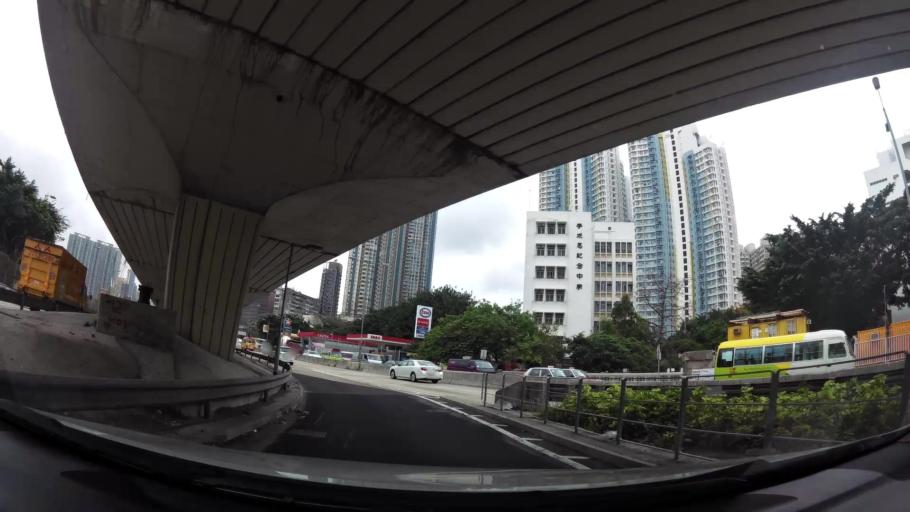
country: HK
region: Kowloon City
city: Kowloon
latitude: 22.3318
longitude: 114.1958
